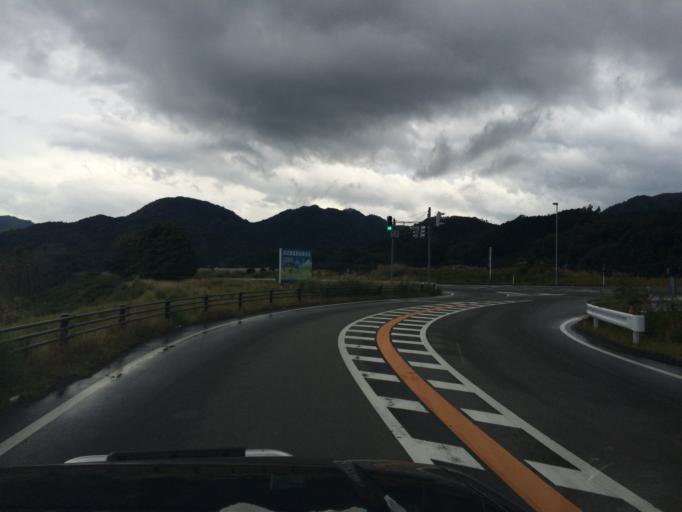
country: JP
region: Hyogo
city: Toyooka
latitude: 35.4481
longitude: 134.7714
